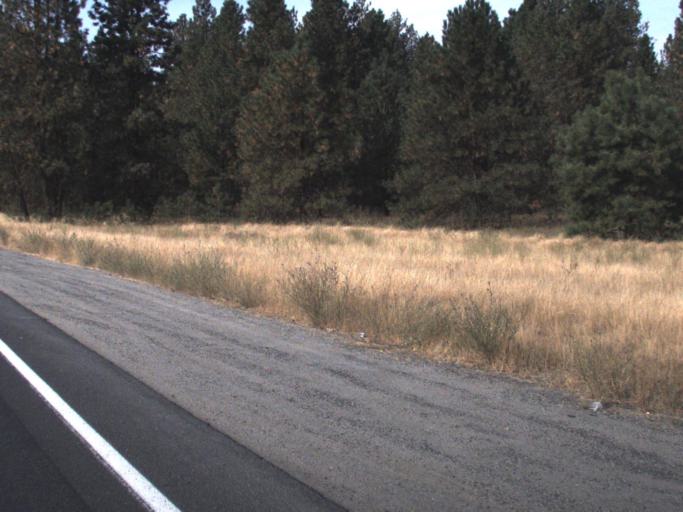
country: US
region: Washington
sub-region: Spokane County
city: Fairwood
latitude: 47.7815
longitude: -117.5331
